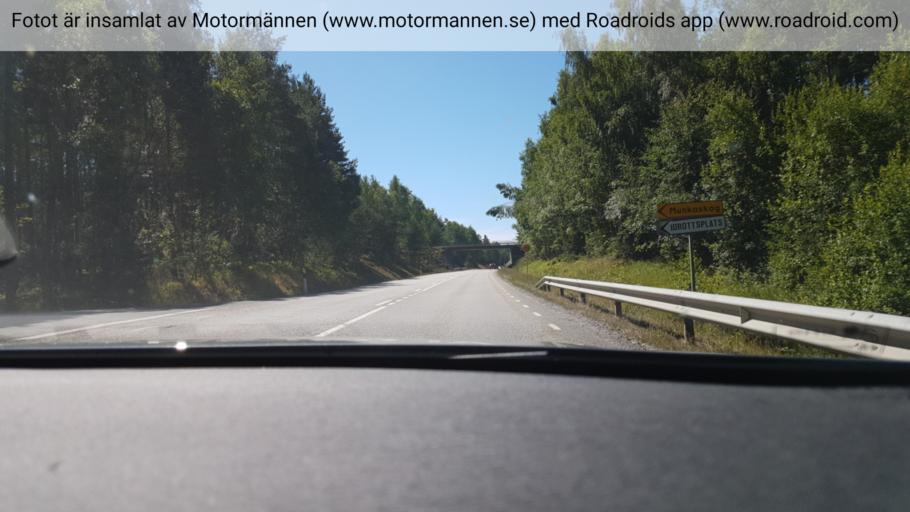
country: SE
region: Joenkoeping
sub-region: Habo Kommun
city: Habo
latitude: 57.9175
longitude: 14.0990
